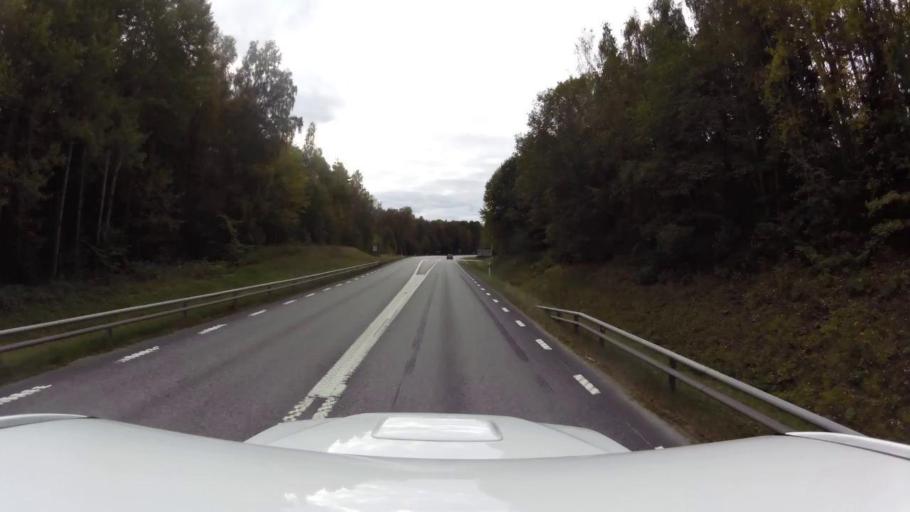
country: SE
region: OEstergoetland
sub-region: Kinda Kommun
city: Rimforsa
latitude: 58.1635
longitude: 15.6799
